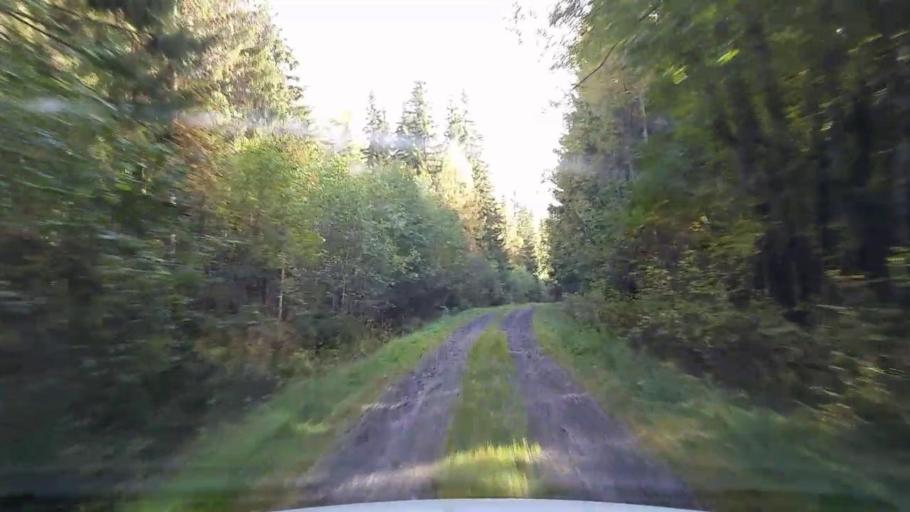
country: SE
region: Gaevleborg
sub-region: Ljusdals Kommun
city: Jaervsoe
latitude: 61.7804
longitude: 16.1803
